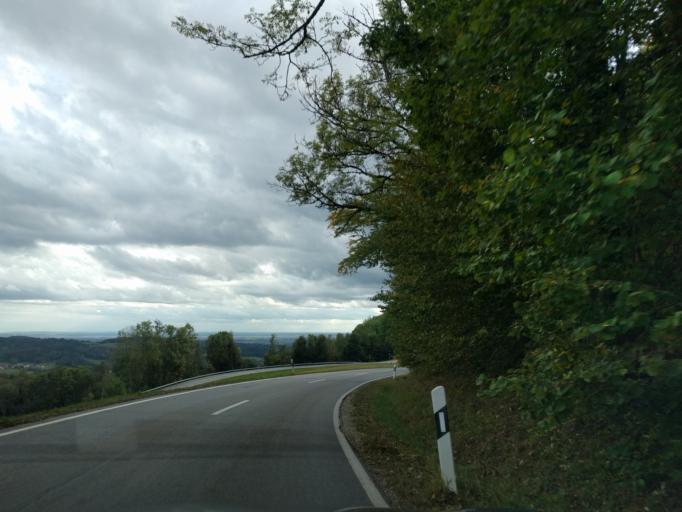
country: DE
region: Bavaria
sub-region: Lower Bavaria
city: Grafling
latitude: 48.8742
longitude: 12.9839
